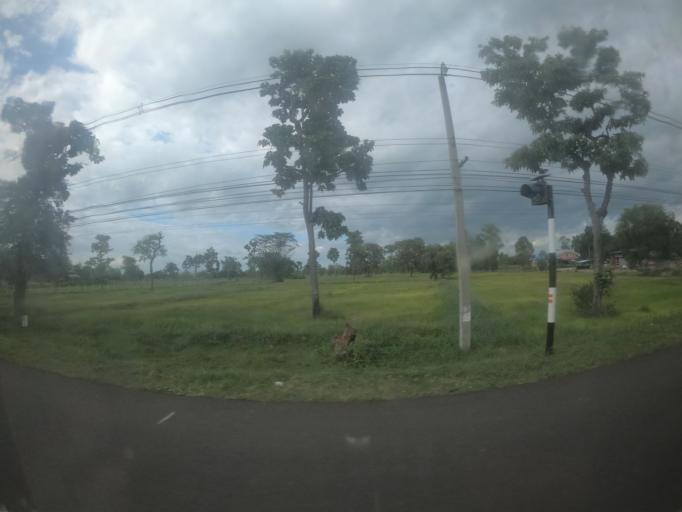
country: TH
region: Surin
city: Kap Choeng
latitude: 14.5520
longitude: 103.5081
